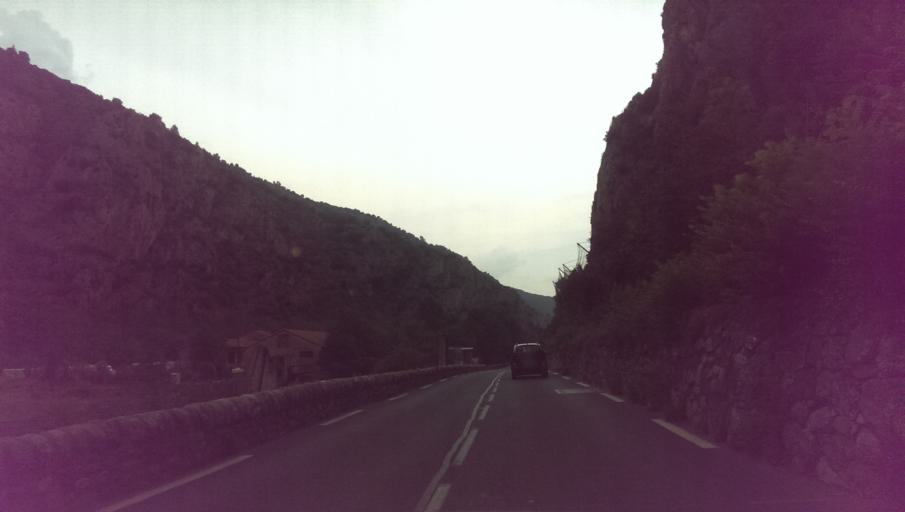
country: FR
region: Languedoc-Roussillon
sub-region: Departement des Pyrenees-Orientales
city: Ria-Sirach
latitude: 42.5923
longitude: 2.3723
